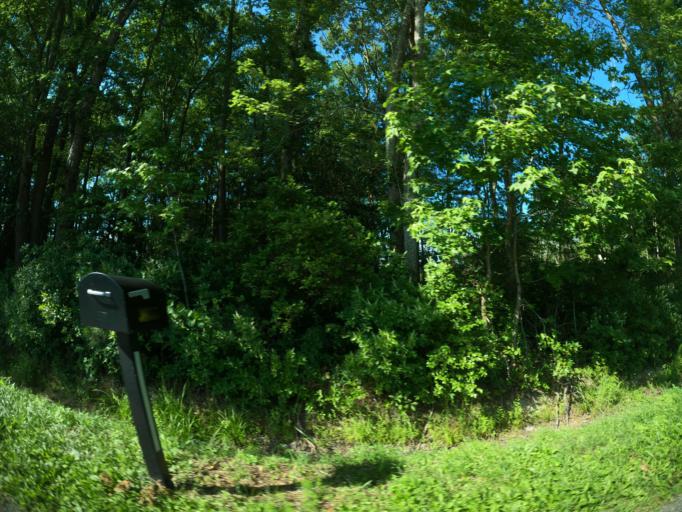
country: US
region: Delaware
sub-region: Sussex County
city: Ocean View
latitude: 38.4890
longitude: -75.1193
